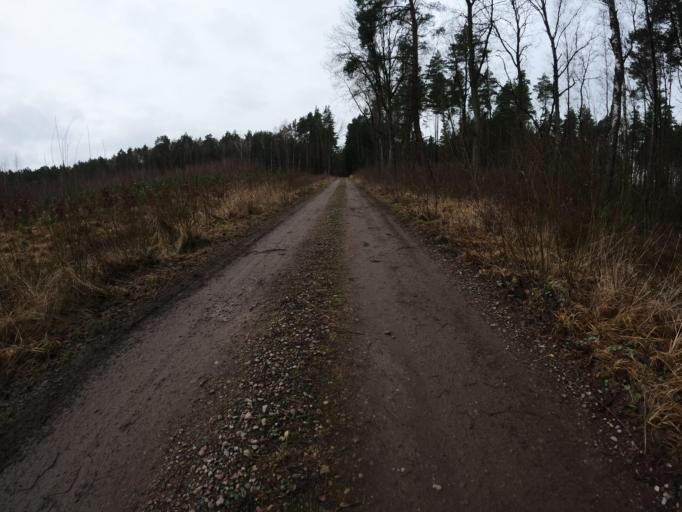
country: PL
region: West Pomeranian Voivodeship
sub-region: Powiat slawienski
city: Darlowo
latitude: 54.4189
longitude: 16.4713
